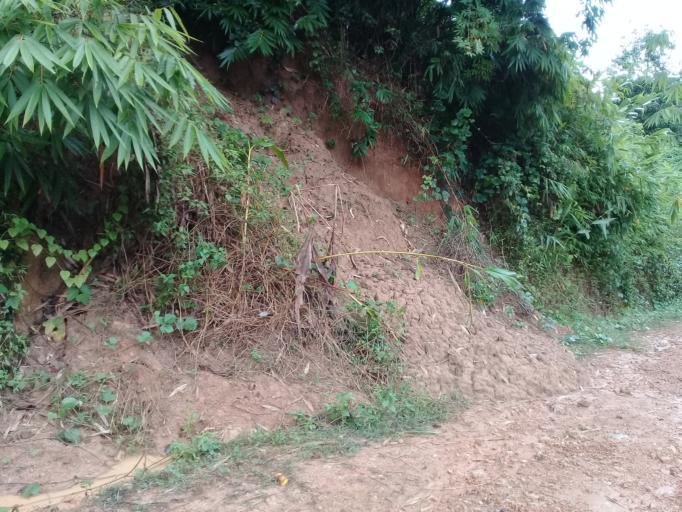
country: VN
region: Huyen Dien Bien
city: Dien Bien Phu
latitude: 21.5525
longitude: 102.8465
